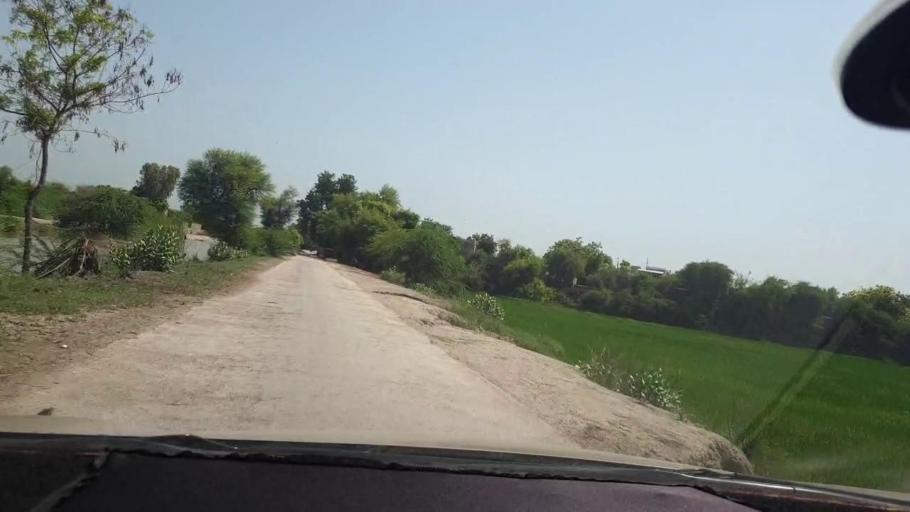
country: PK
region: Sindh
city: Kambar
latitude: 27.5089
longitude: 68.0123
